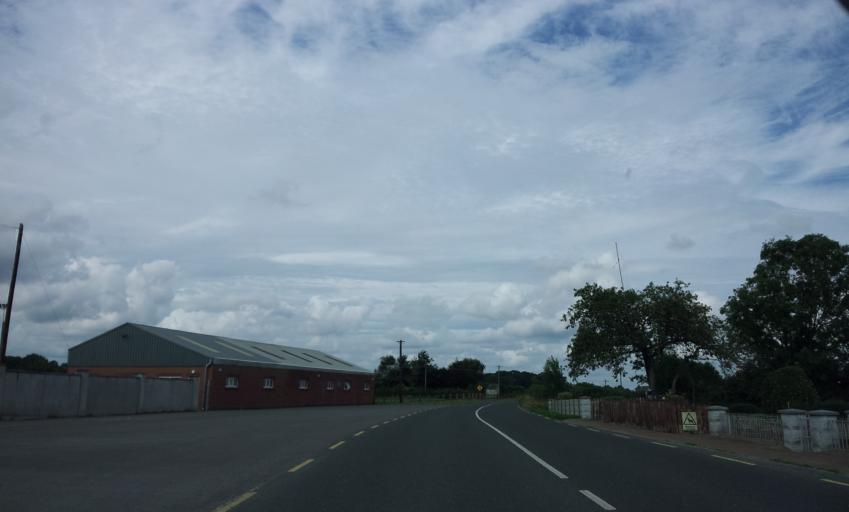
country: IE
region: Leinster
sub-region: Laois
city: Stradbally
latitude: 52.9692
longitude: -7.2106
